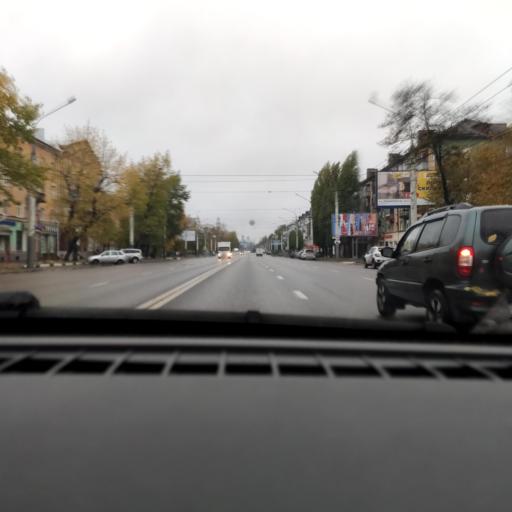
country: RU
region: Voronezj
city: Voronezh
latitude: 51.6386
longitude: 39.2351
